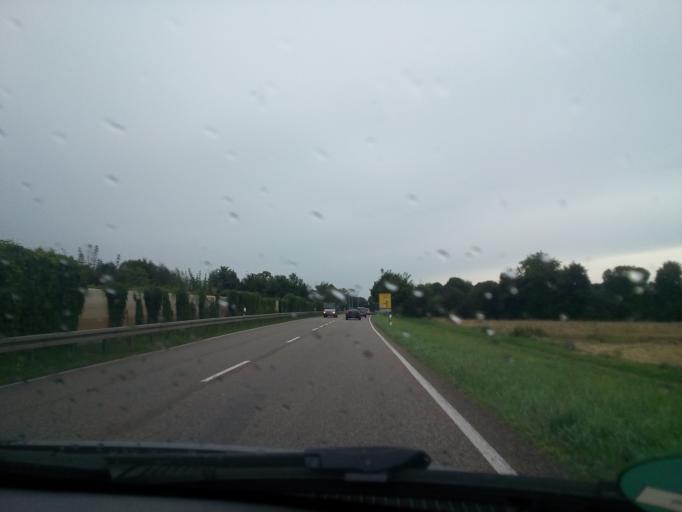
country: DE
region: Baden-Wuerttemberg
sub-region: Karlsruhe Region
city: Buhl
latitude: 48.6992
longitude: 8.1214
